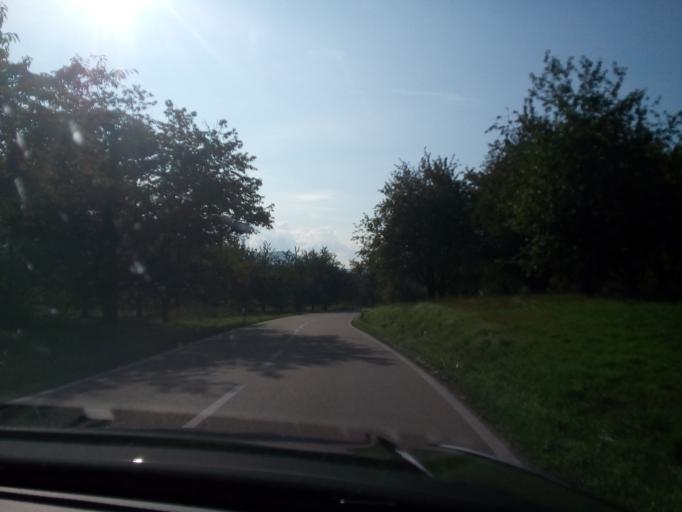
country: DE
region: Baden-Wuerttemberg
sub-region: Freiburg Region
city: Haslach
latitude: 48.5651
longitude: 8.0425
